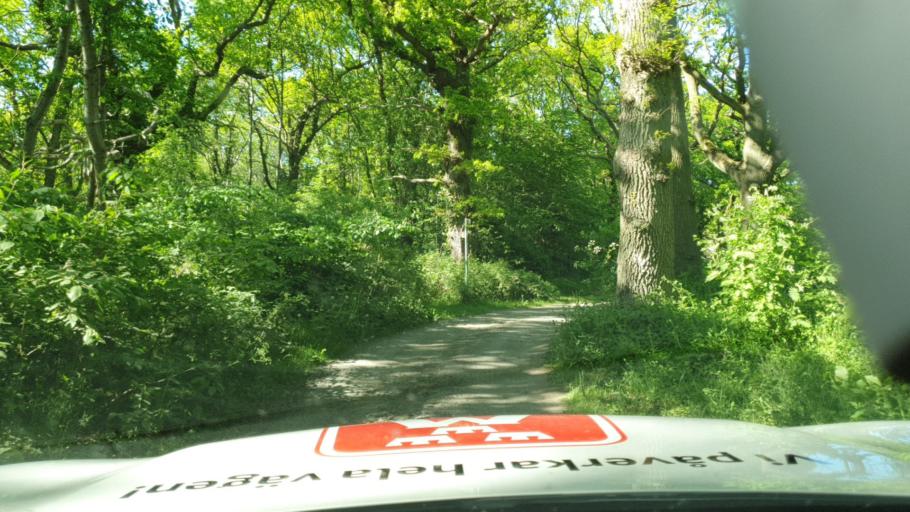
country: SE
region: Skane
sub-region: Simrishamns Kommun
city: Simrishamn
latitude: 55.4936
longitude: 14.2742
